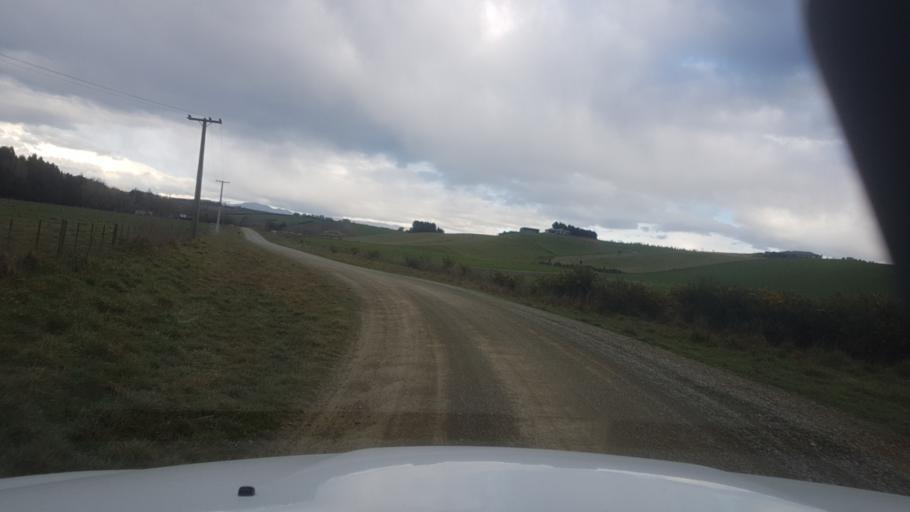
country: NZ
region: Canterbury
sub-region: Timaru District
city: Pleasant Point
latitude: -44.3378
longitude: 171.1791
